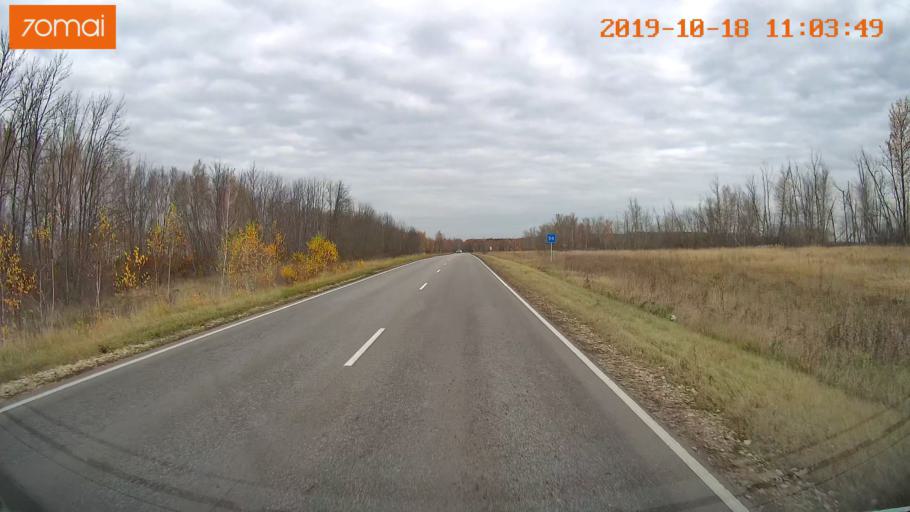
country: RU
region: Tula
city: Yepifan'
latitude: 53.8855
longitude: 38.5496
